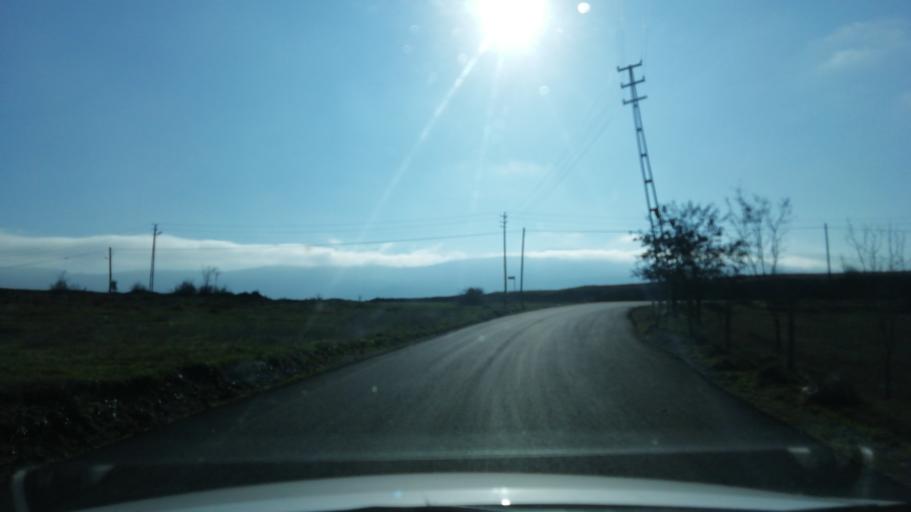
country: TR
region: Karabuk
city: Safranbolu
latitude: 41.2293
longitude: 32.7879
